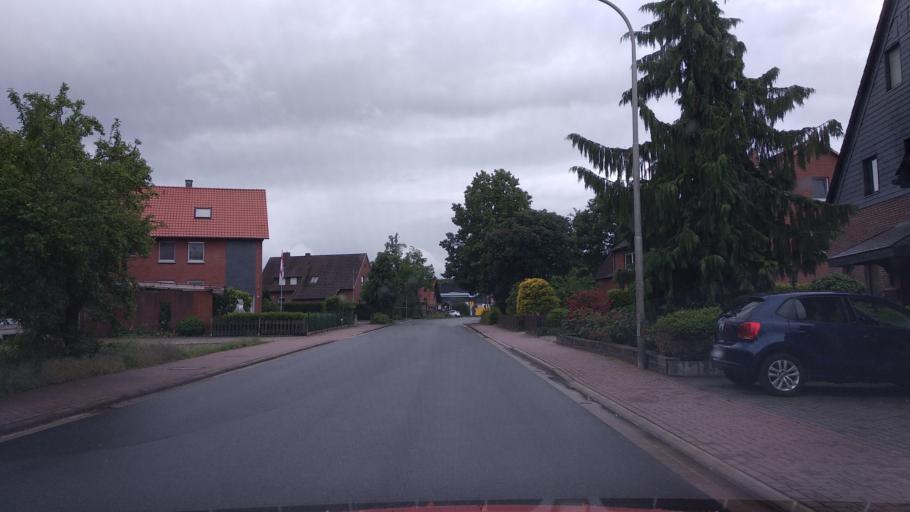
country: DE
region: Lower Saxony
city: Auhagen
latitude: 52.3952
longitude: 9.2870
